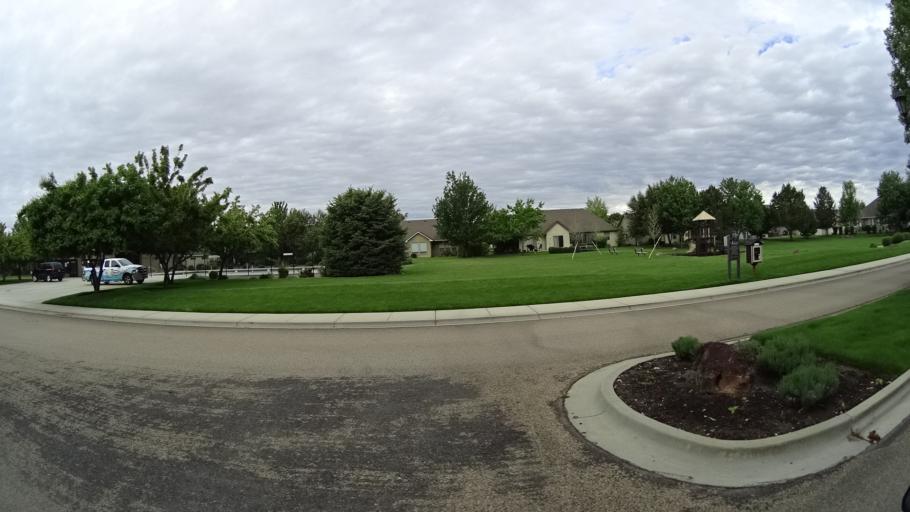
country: US
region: Idaho
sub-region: Ada County
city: Star
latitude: 43.6901
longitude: -116.5053
